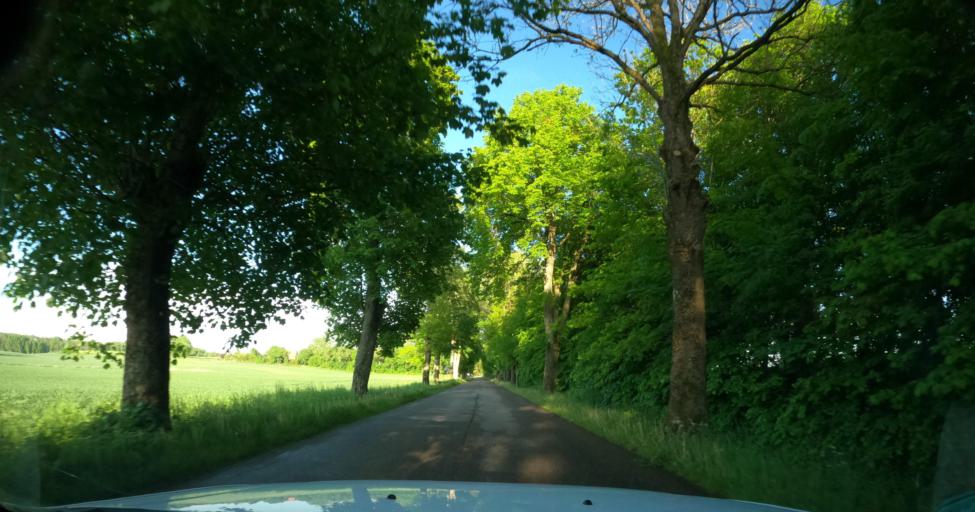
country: PL
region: Warmian-Masurian Voivodeship
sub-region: Powiat braniewski
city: Pieniezno
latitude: 54.2546
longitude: 19.9758
